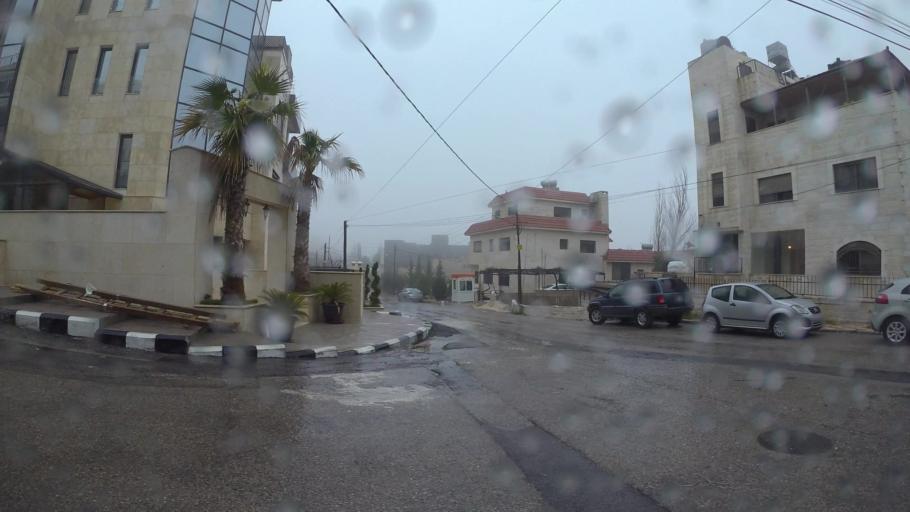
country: JO
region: Amman
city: Wadi as Sir
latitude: 31.9974
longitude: 35.8233
